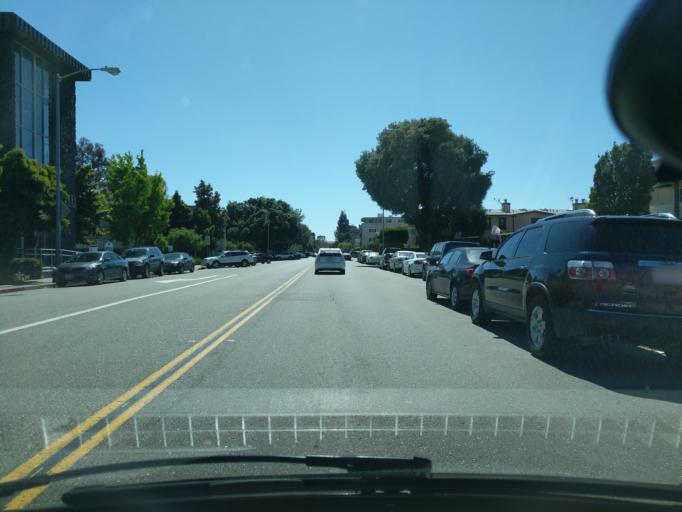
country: US
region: California
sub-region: Alameda County
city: San Leandro
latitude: 37.7272
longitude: -122.1517
